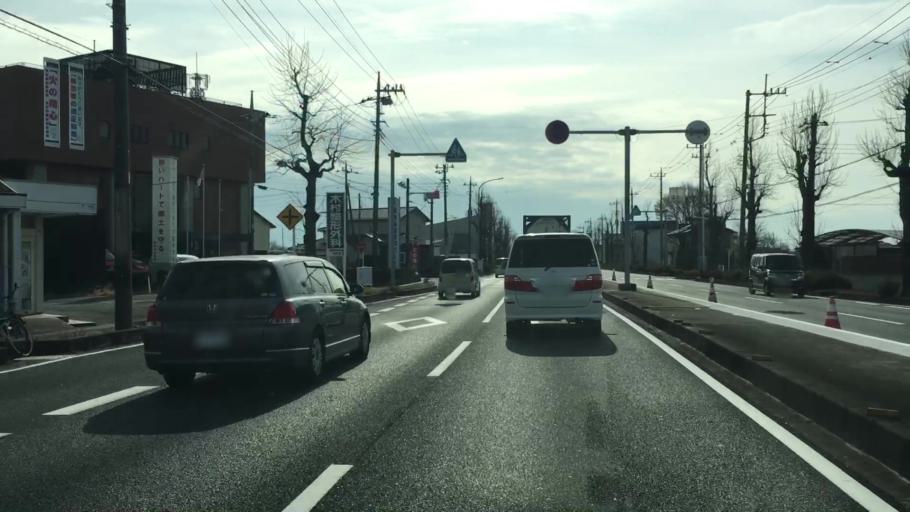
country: JP
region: Saitama
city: Kumagaya
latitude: 36.1685
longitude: 139.3706
